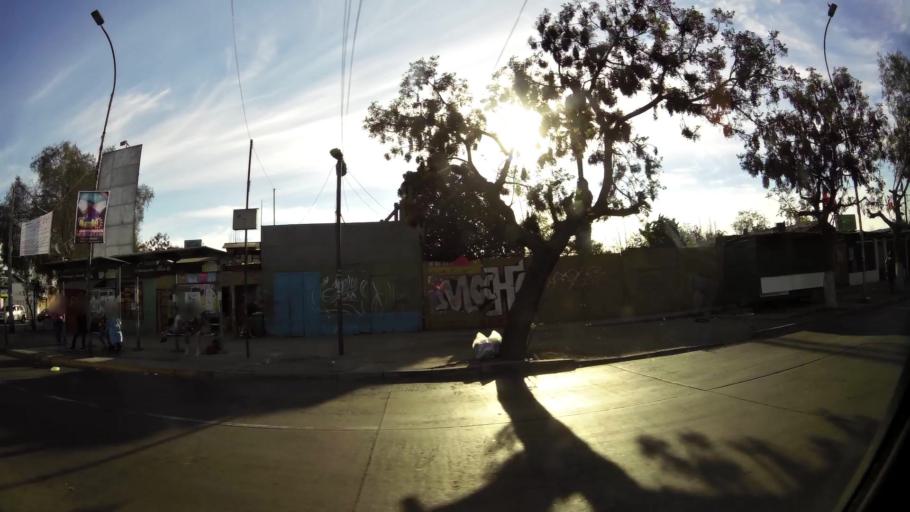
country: CL
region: Santiago Metropolitan
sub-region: Provincia de Santiago
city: Lo Prado
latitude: -33.4412
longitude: -70.7074
